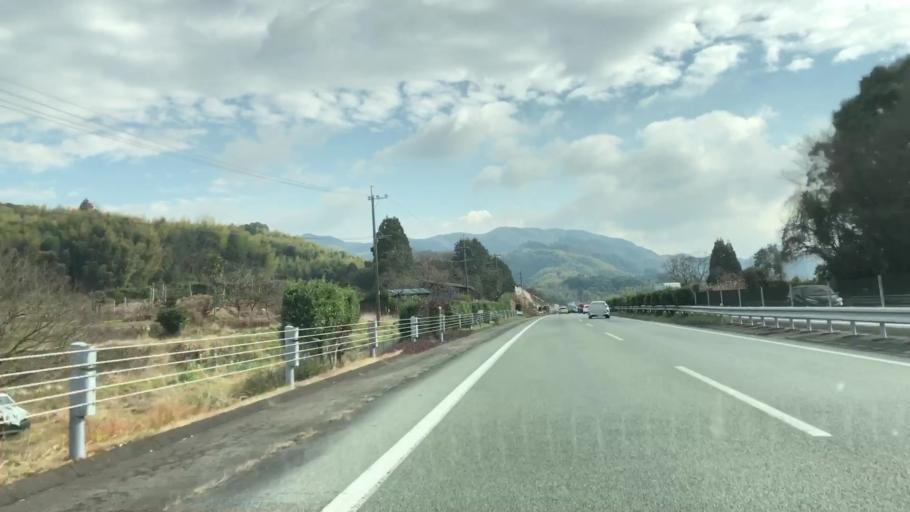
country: JP
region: Fukuoka
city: Setakamachi-takayanagi
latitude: 33.1181
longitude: 130.5251
